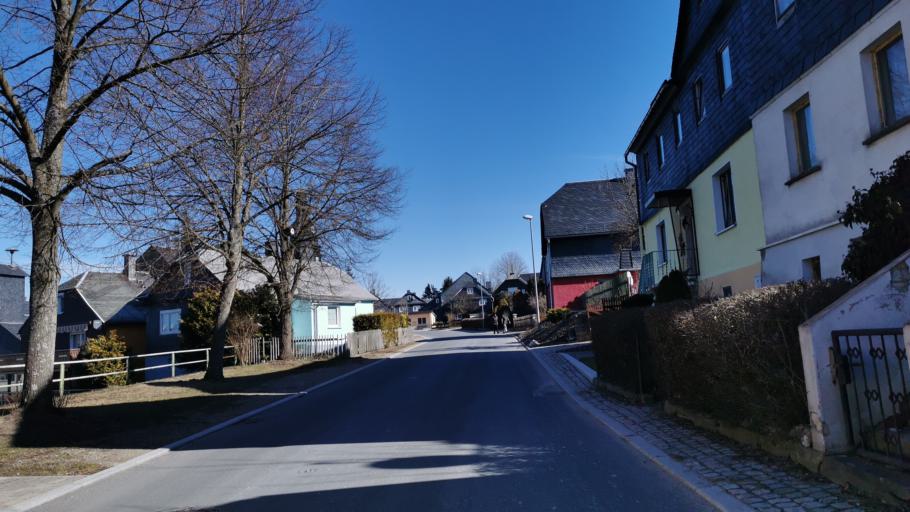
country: DE
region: Thuringia
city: Wurzbach
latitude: 50.5031
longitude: 11.4958
